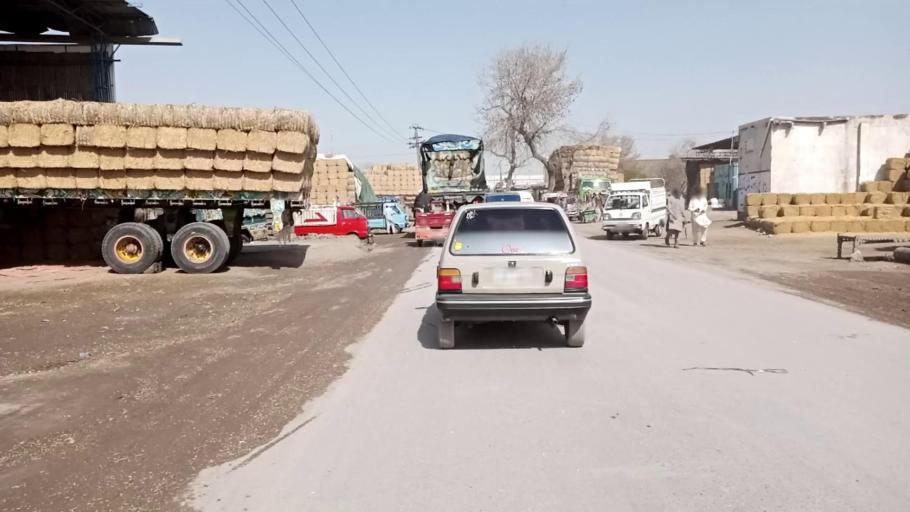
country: PK
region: Khyber Pakhtunkhwa
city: Peshawar
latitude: 34.0176
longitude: 71.6467
